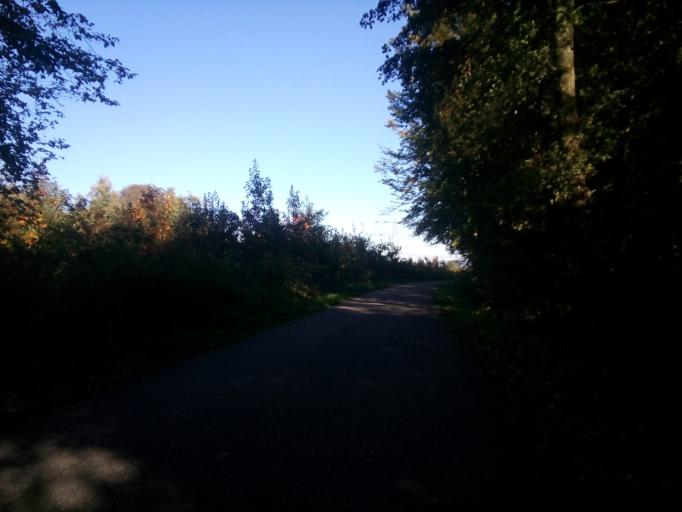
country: DE
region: Baden-Wuerttemberg
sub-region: Karlsruhe Region
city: Zell
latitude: 48.6956
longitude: 8.0368
